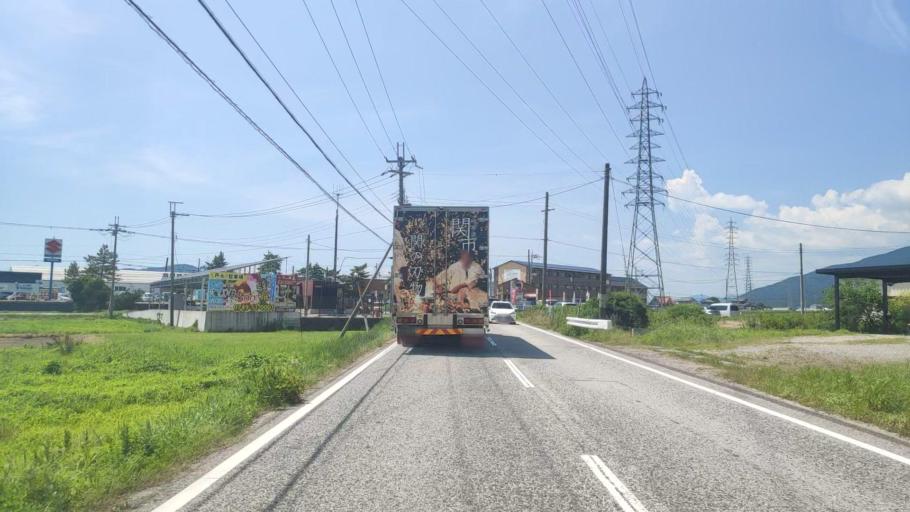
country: JP
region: Shiga Prefecture
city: Nagahama
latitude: 35.3850
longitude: 136.3668
